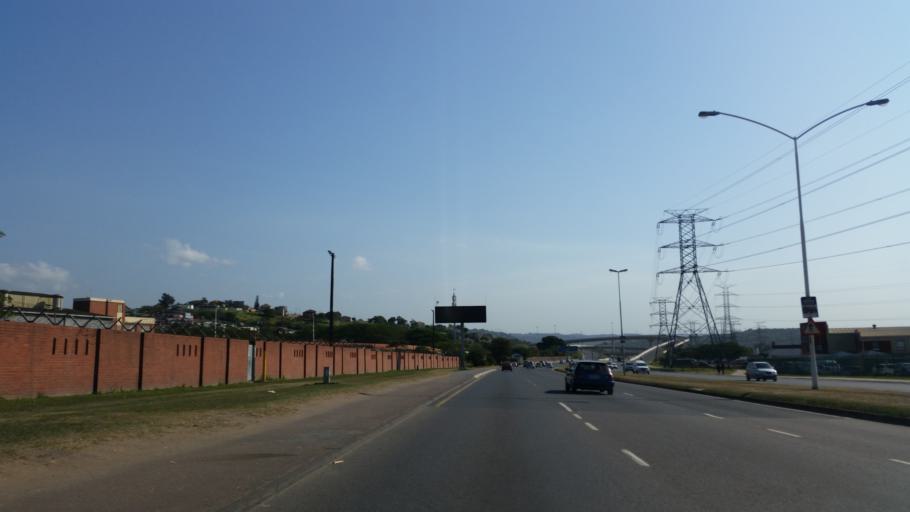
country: ZA
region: KwaZulu-Natal
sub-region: eThekwini Metropolitan Municipality
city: Berea
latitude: -29.8105
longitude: 30.9863
